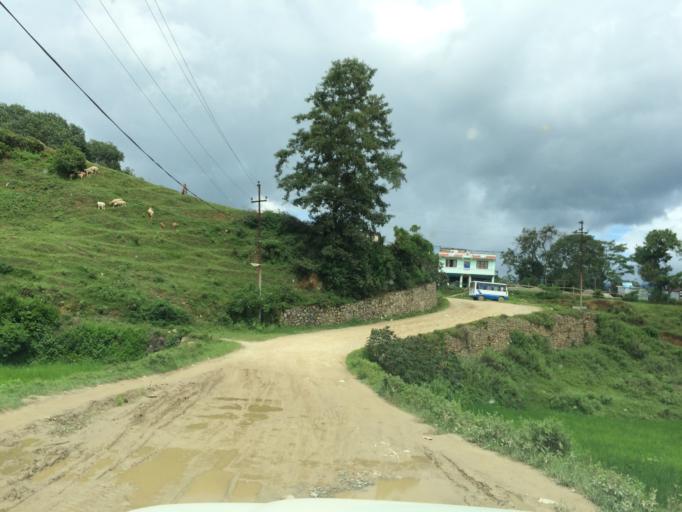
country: NP
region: Central Region
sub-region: Bagmati Zone
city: Patan
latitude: 27.6014
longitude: 85.3119
